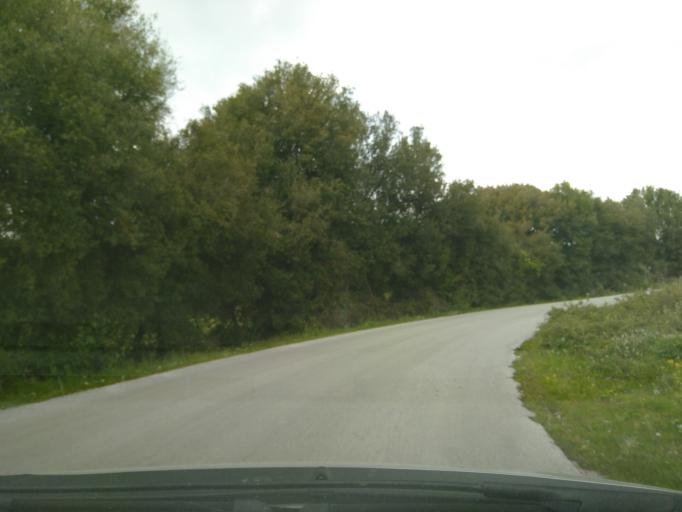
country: GR
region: Epirus
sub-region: Nomos Ioanninon
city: Asprangeloi
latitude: 39.7727
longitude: 20.6973
